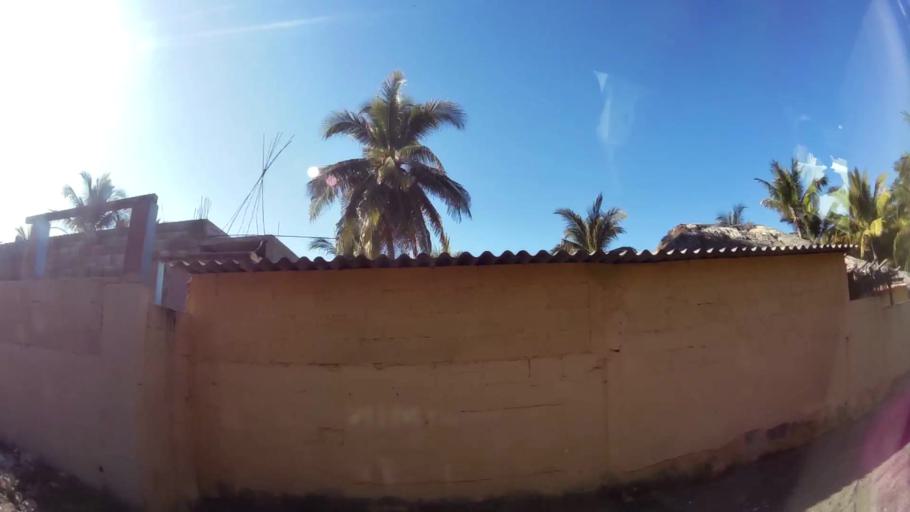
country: GT
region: Santa Rosa
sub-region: Municipio de Taxisco
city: Taxisco
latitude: 13.8917
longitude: -90.4881
